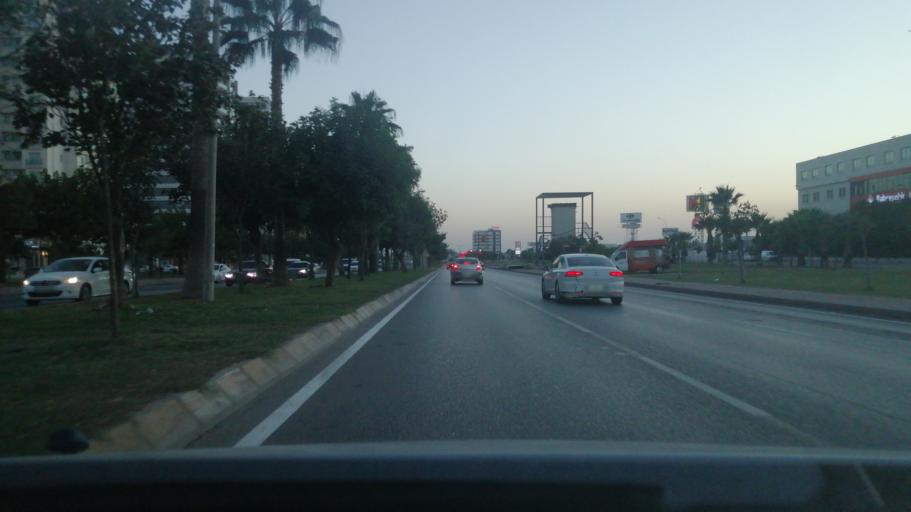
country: TR
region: Adana
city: Seyhan
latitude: 37.0197
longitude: 35.2524
